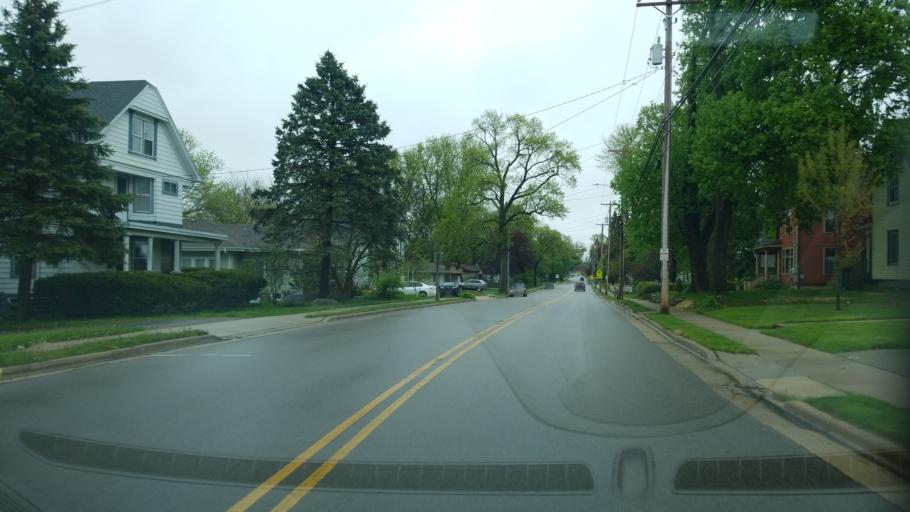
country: US
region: Wisconsin
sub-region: Dane County
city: Oregon
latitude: 42.9289
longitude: -89.3919
